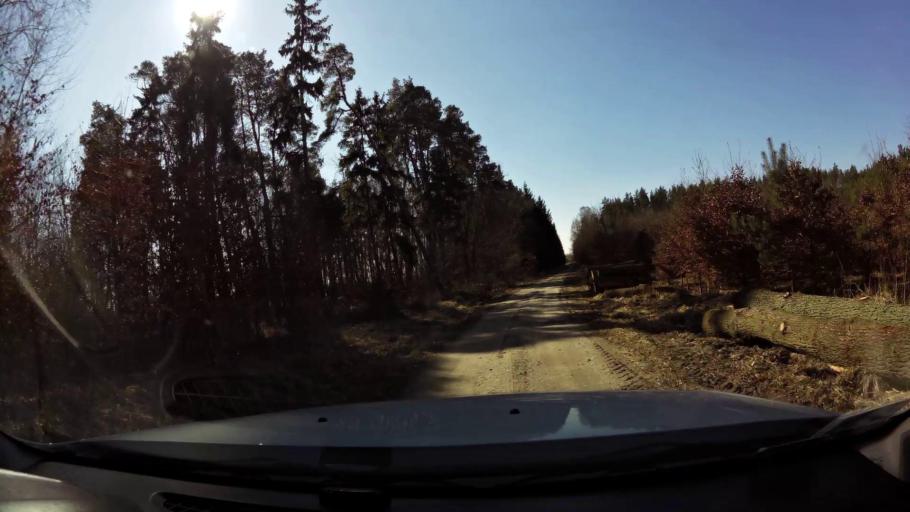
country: PL
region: West Pomeranian Voivodeship
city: Trzcinsko Zdroj
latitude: 53.0010
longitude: 14.6126
